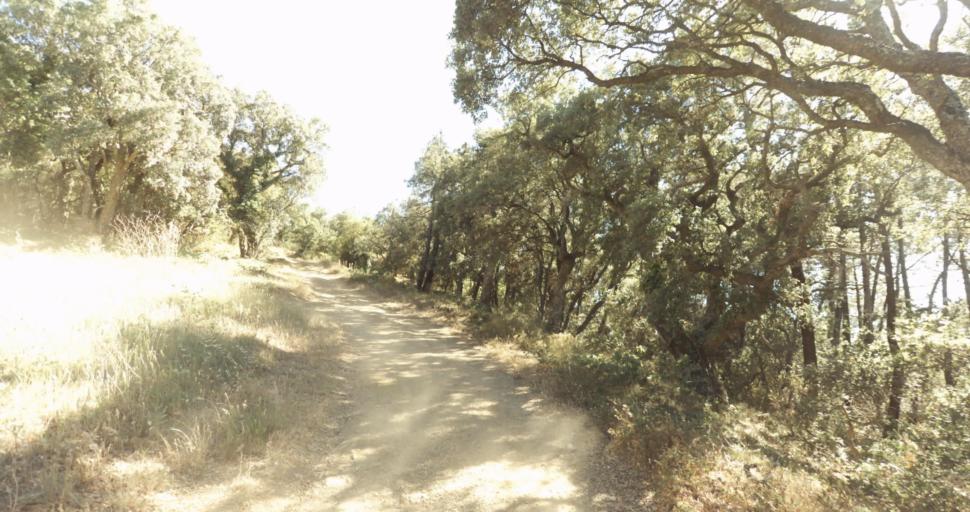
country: FR
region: Provence-Alpes-Cote d'Azur
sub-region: Departement du Var
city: Gassin
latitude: 43.2425
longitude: 6.5837
